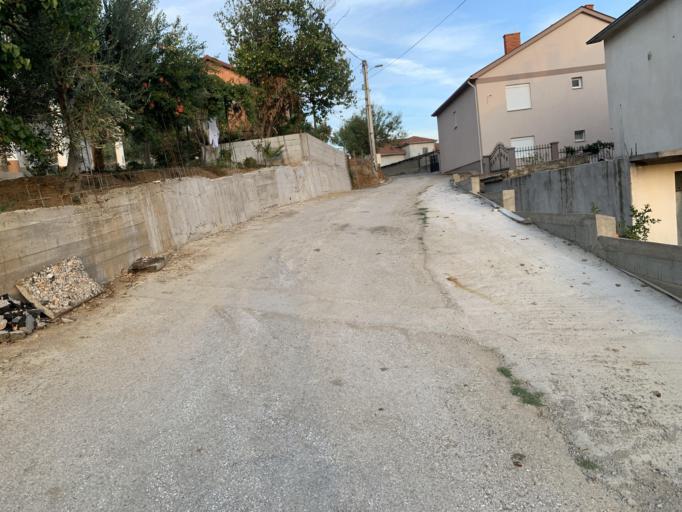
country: MK
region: Bogdanci
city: Bogdanci
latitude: 41.2063
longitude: 22.5783
